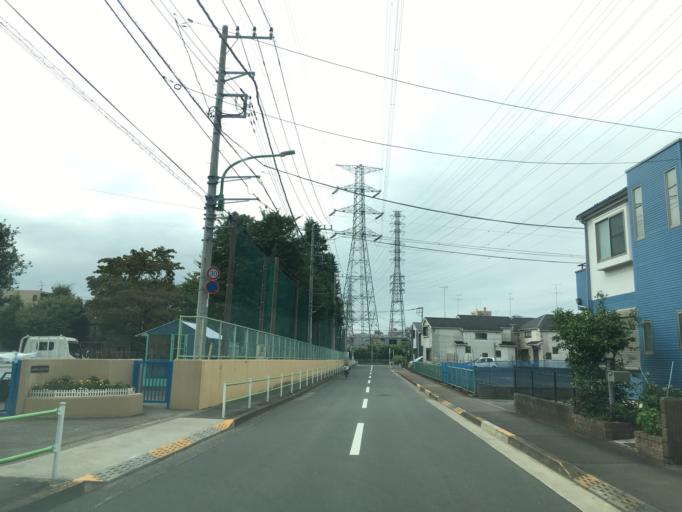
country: JP
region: Tokyo
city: Higashimurayama-shi
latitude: 35.7314
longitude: 139.4410
